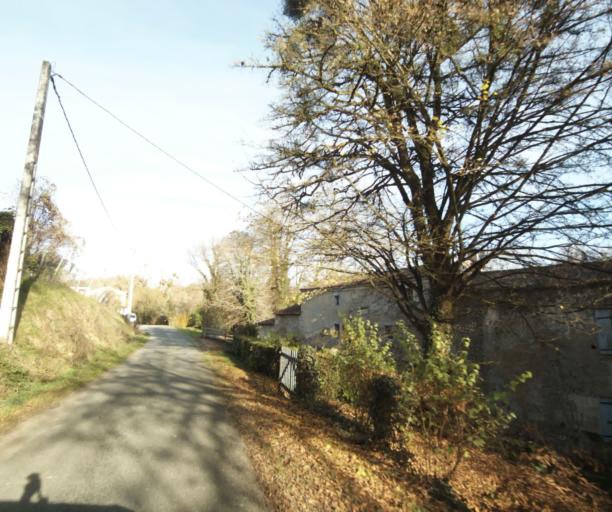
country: FR
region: Poitou-Charentes
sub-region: Departement de la Charente-Maritime
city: Chaniers
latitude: 45.7323
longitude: -0.5382
